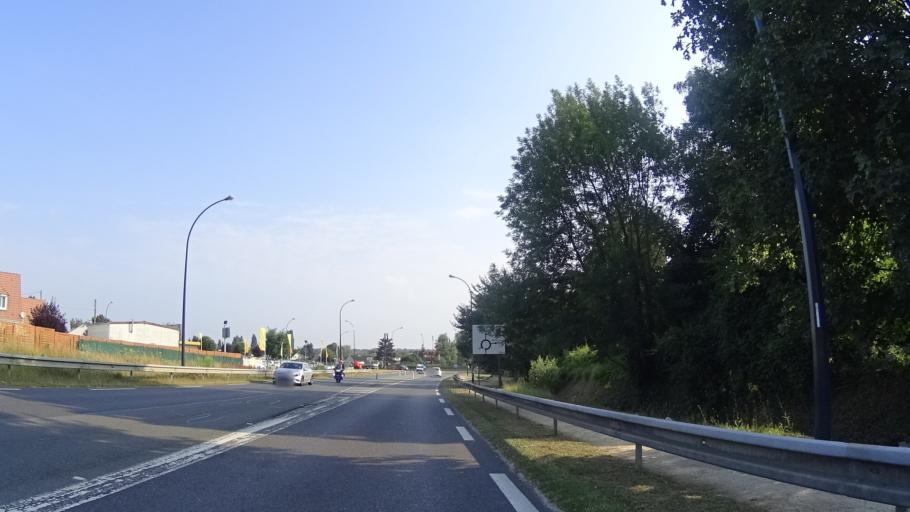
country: FR
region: Ile-de-France
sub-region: Departement du Val-d'Oise
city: Chaumontel
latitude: 49.1218
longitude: 2.4270
